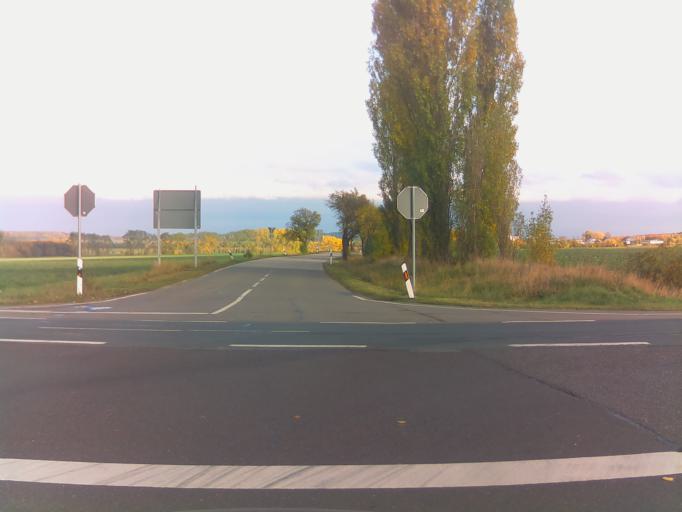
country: DE
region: Thuringia
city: Bosleben-Wullersleben
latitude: 50.8463
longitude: 11.0615
